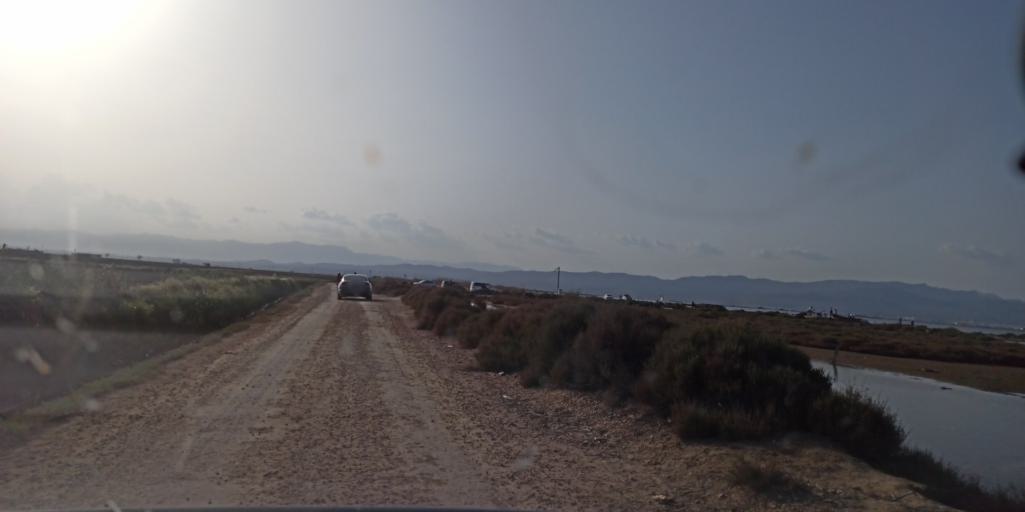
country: ES
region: Catalonia
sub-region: Provincia de Tarragona
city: Deltebre
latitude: 40.7634
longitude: 0.7515
